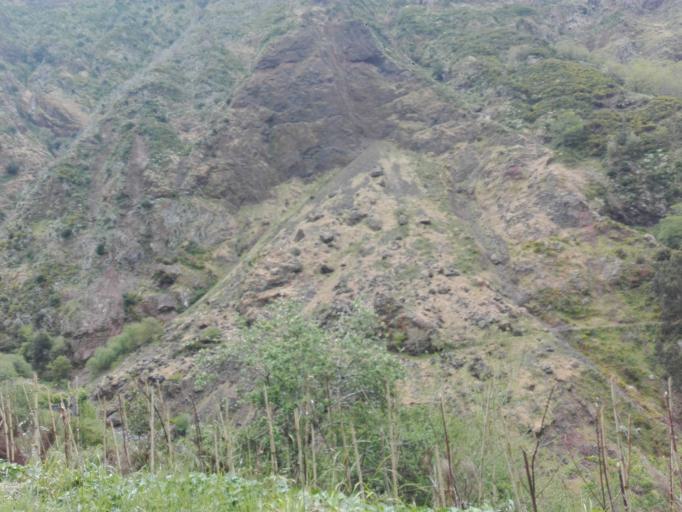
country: PT
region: Madeira
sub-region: Camara de Lobos
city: Curral das Freiras
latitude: 32.7462
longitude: -16.9614
